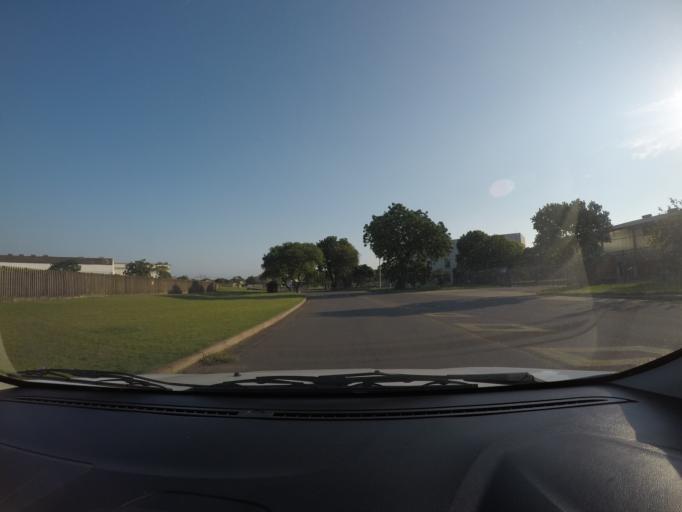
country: ZA
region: KwaZulu-Natal
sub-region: uThungulu District Municipality
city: Richards Bay
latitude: -28.7684
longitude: 32.0096
